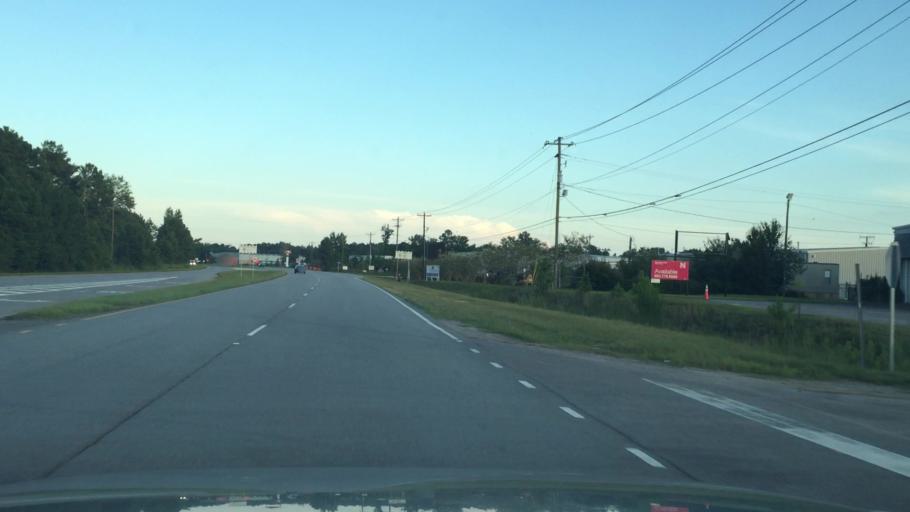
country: US
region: South Carolina
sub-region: Richland County
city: Forest Acres
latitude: 33.9443
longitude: -80.9616
